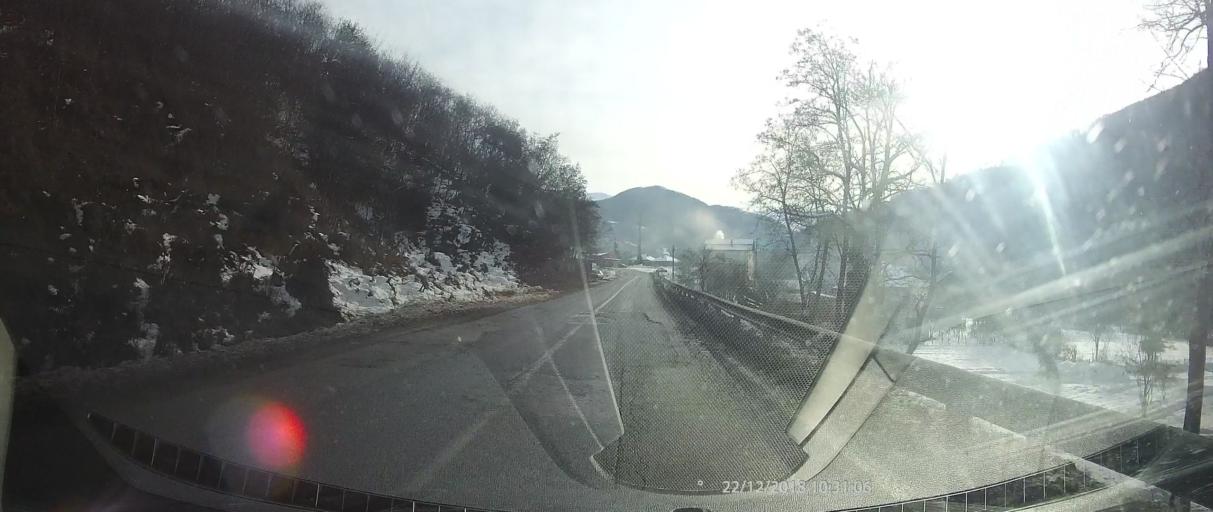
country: MK
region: Kriva Palanka
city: Kriva Palanka
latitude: 42.2237
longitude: 22.4211
